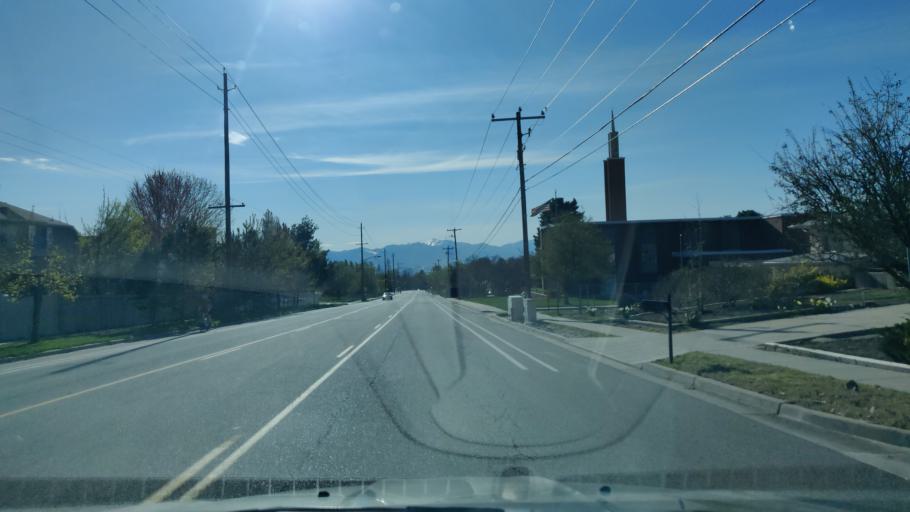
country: US
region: Utah
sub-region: Salt Lake County
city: Cottonwood Heights
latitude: 40.6095
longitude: -111.8088
